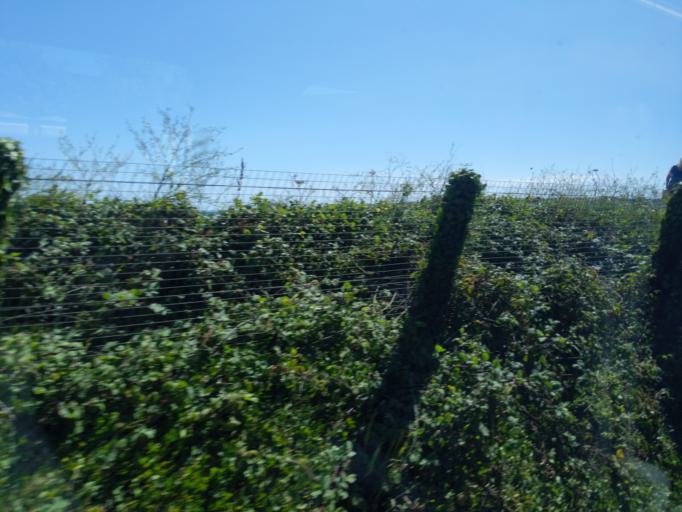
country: GB
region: England
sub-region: Cornwall
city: Penzance
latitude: 50.1276
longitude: -5.5128
